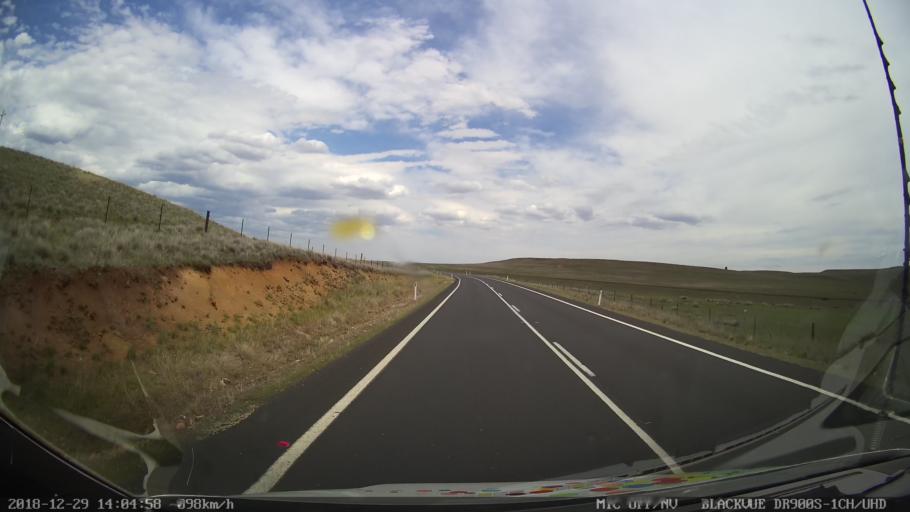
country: AU
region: New South Wales
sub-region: Cooma-Monaro
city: Cooma
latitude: -36.3237
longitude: 149.1888
